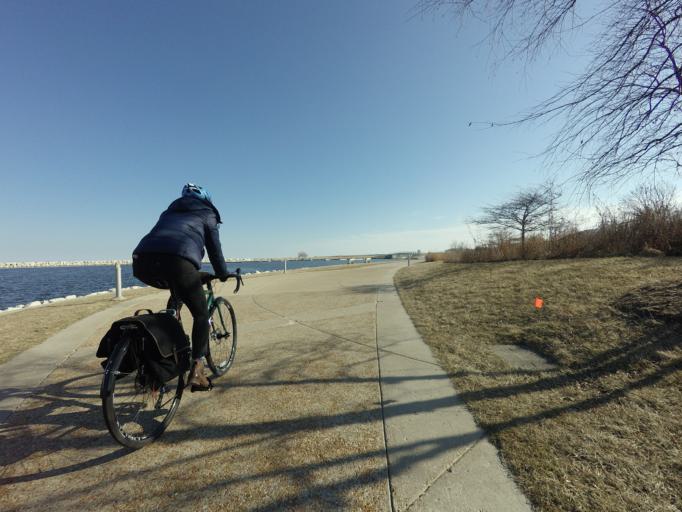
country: US
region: Wisconsin
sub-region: Milwaukee County
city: Milwaukee
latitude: 43.0363
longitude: -87.8971
